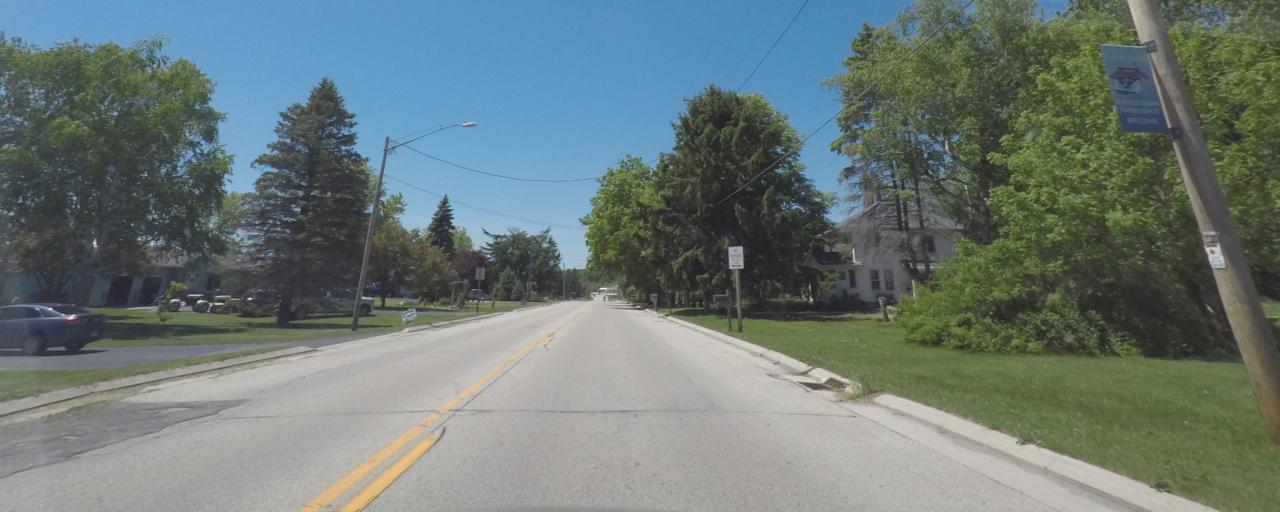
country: US
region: Wisconsin
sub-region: Sheboygan County
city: Plymouth
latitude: 43.6555
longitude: -88.0134
